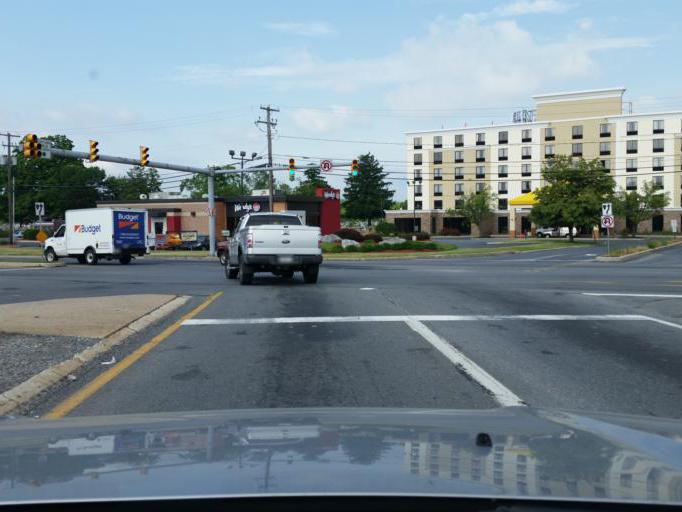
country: US
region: Pennsylvania
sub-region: Dauphin County
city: Highspire
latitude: 40.2178
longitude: -76.7904
